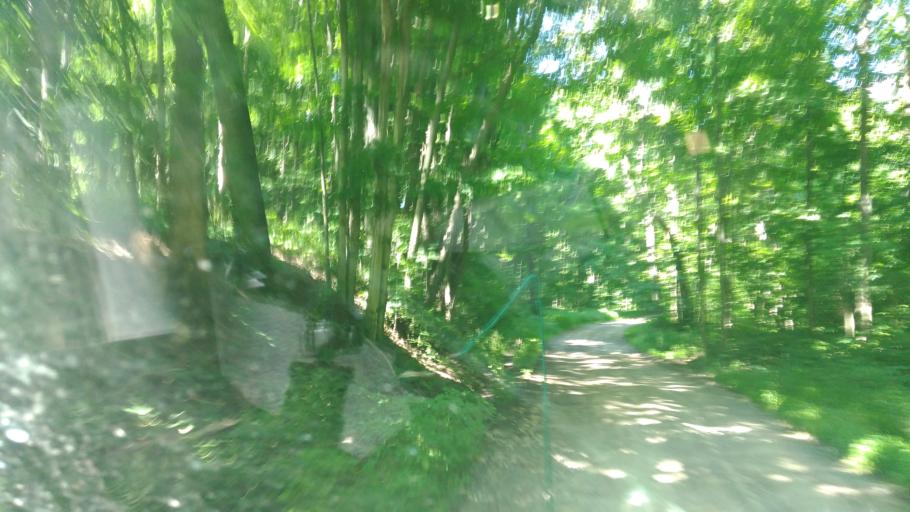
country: US
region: New York
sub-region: Wayne County
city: Clyde
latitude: 43.0253
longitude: -76.8706
